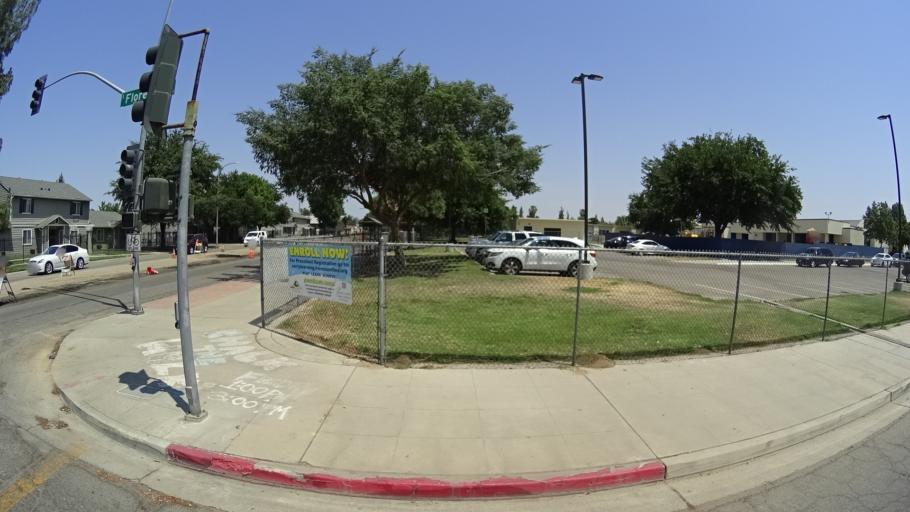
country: US
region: California
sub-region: Fresno County
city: Fresno
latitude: 36.7178
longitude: -119.7997
